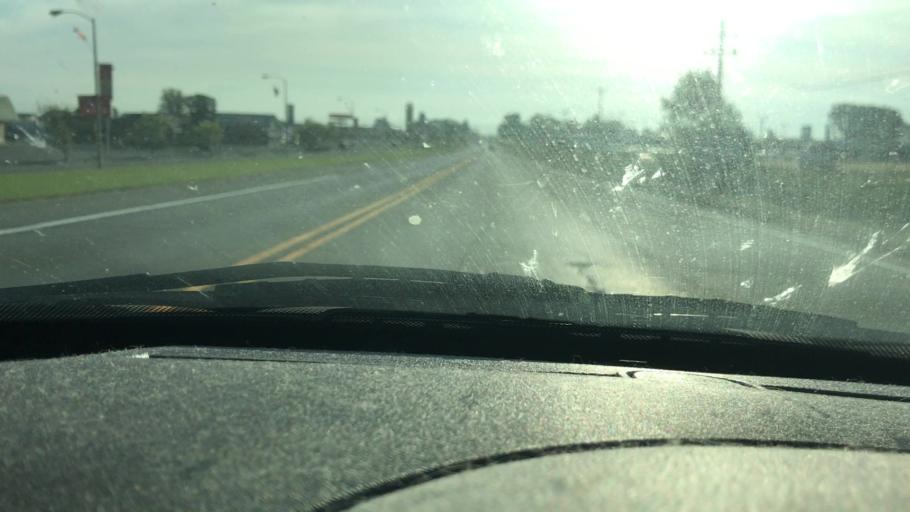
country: US
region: Wisconsin
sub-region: Outagamie County
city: Seymour
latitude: 44.5006
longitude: -88.3257
